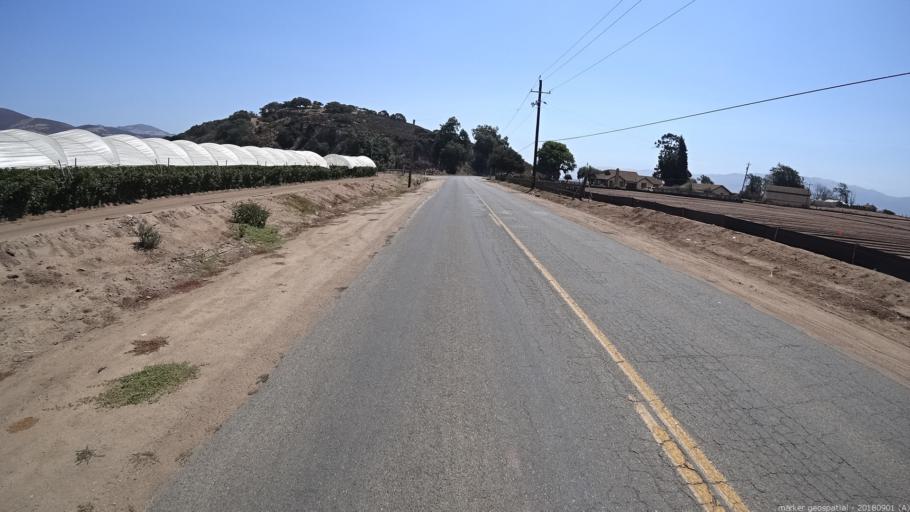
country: US
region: California
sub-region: Monterey County
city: Salinas
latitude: 36.6937
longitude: -121.5701
